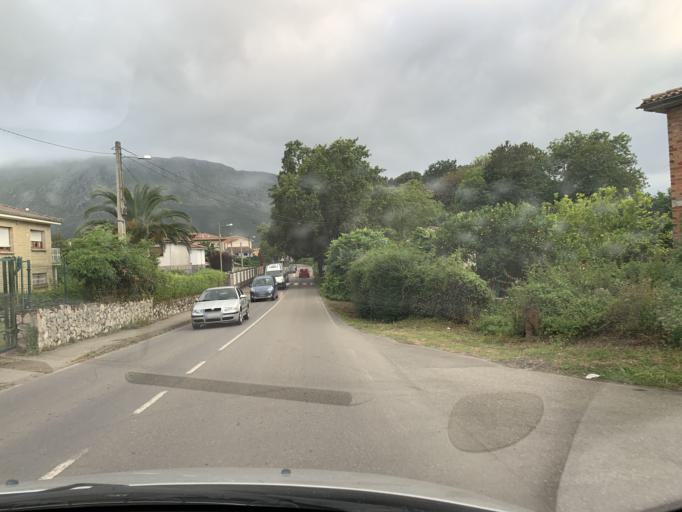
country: ES
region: Asturias
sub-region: Province of Asturias
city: Llanes
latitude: 43.4305
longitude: -4.8619
